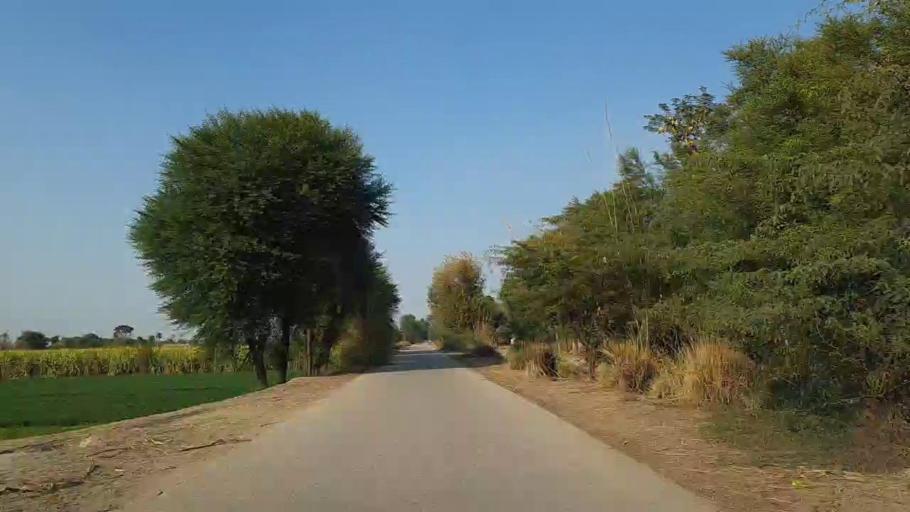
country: PK
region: Sindh
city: Daur
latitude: 26.4117
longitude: 68.2592
